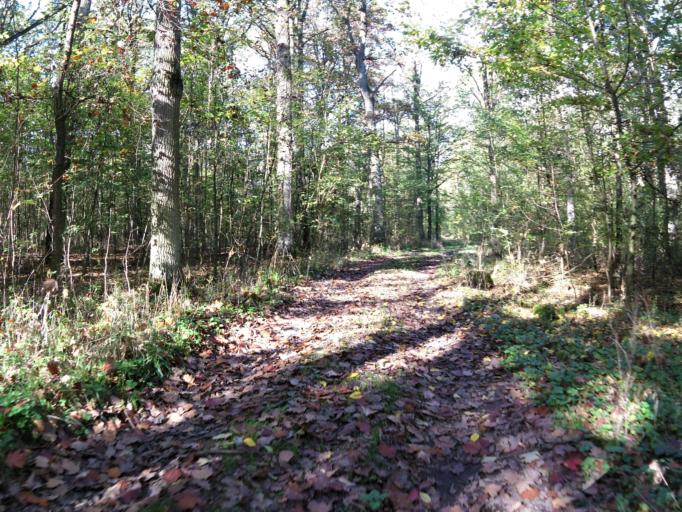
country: DE
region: Bavaria
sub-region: Regierungsbezirk Unterfranken
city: Sulzfeld am Main
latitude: 49.7132
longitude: 10.0991
